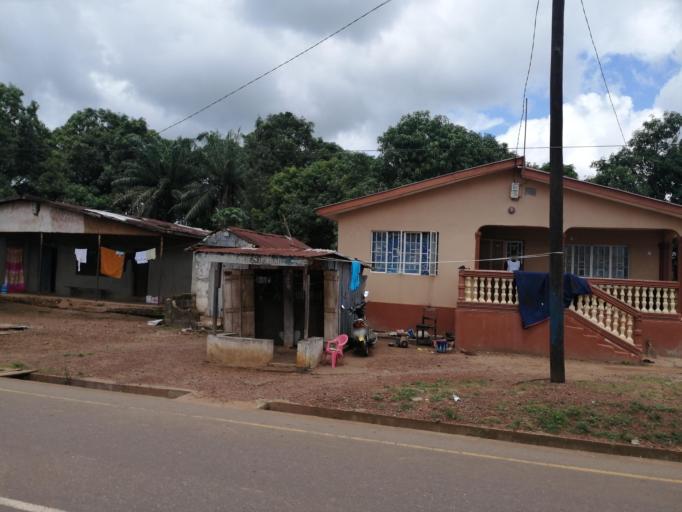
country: SL
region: Northern Province
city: Port Loko
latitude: 8.7703
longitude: -12.7784
